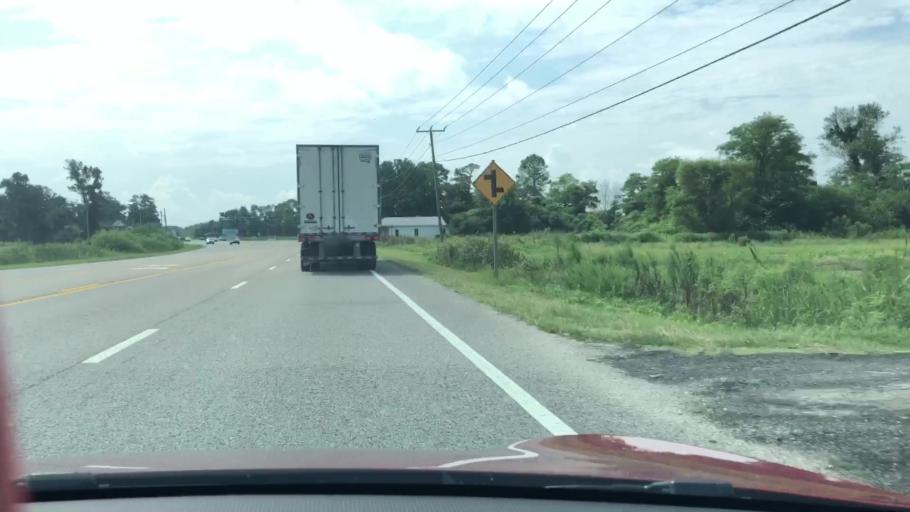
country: US
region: North Carolina
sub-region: Dare County
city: Southern Shores
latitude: 36.2049
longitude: -75.8664
